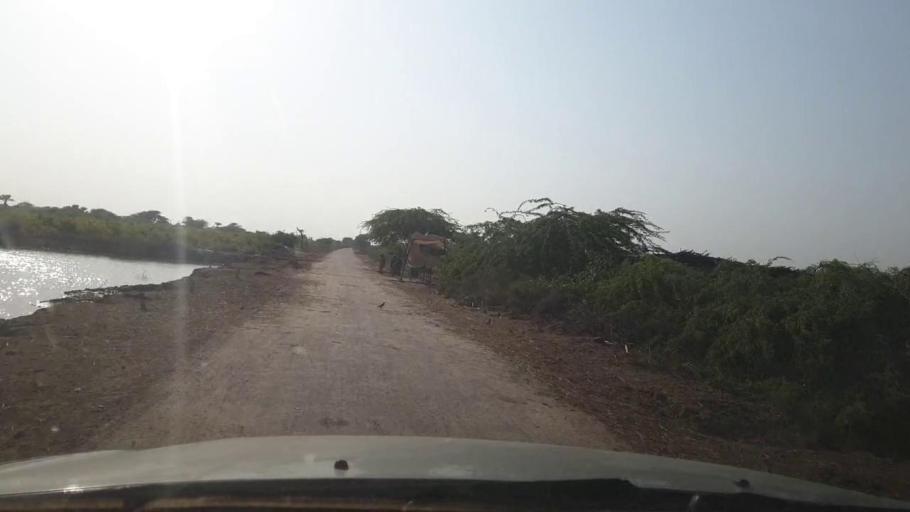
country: PK
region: Sindh
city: Tando Ghulam Ali
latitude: 25.1892
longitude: 68.9476
